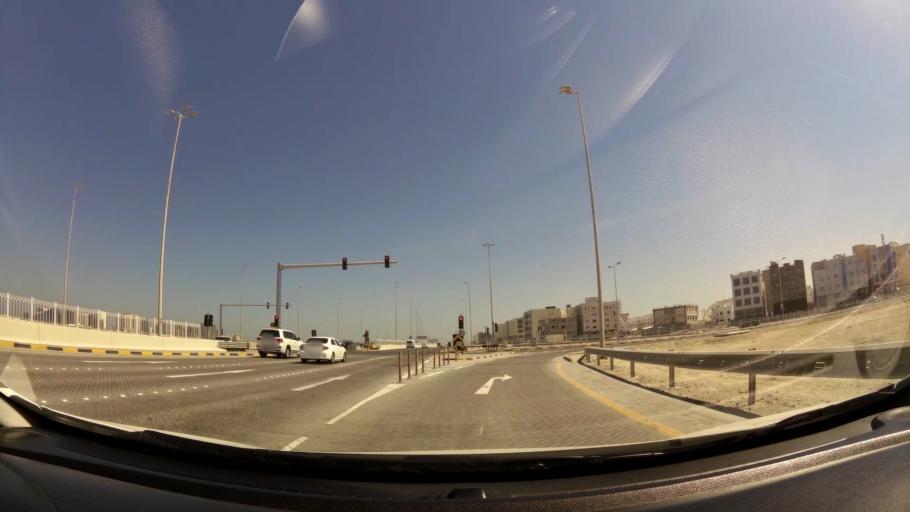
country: BH
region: Muharraq
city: Al Hadd
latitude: 26.2839
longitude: 50.6447
